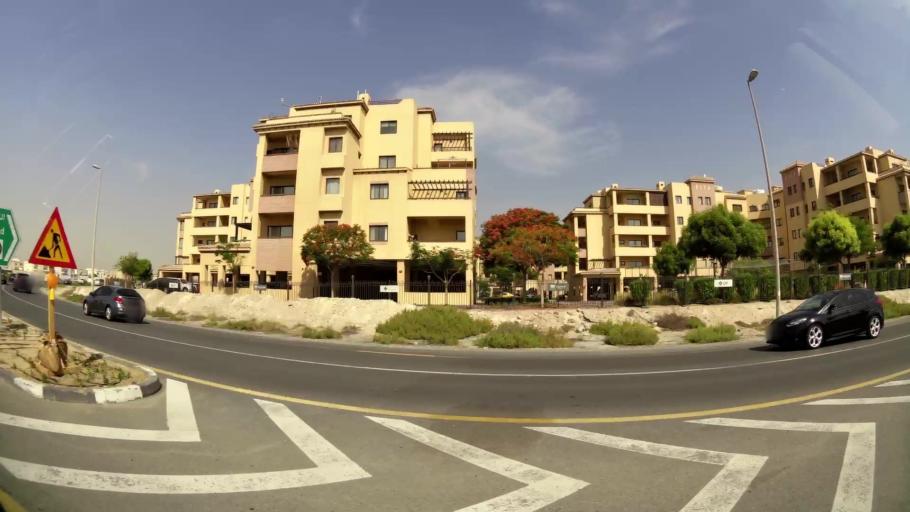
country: AE
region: Ash Shariqah
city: Sharjah
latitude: 25.2108
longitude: 55.4214
